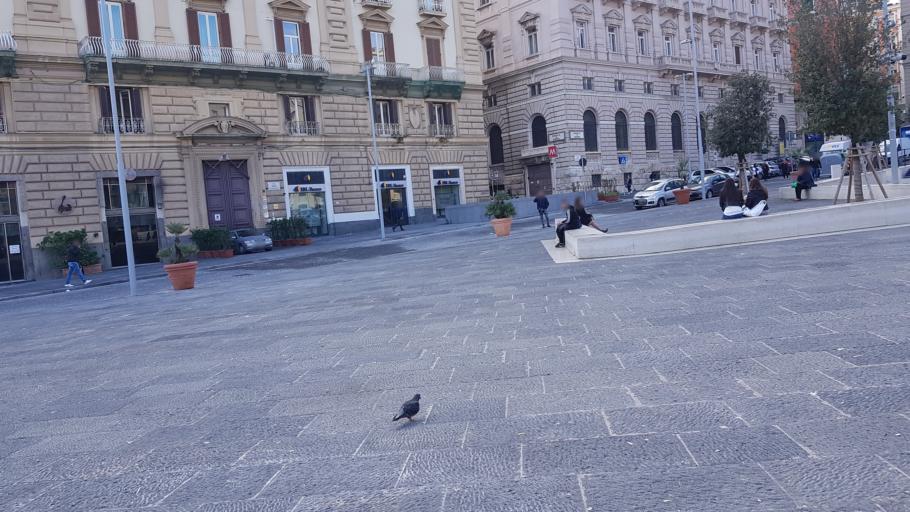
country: IT
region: Campania
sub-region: Provincia di Napoli
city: Napoli
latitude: 40.8399
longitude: 14.2518
